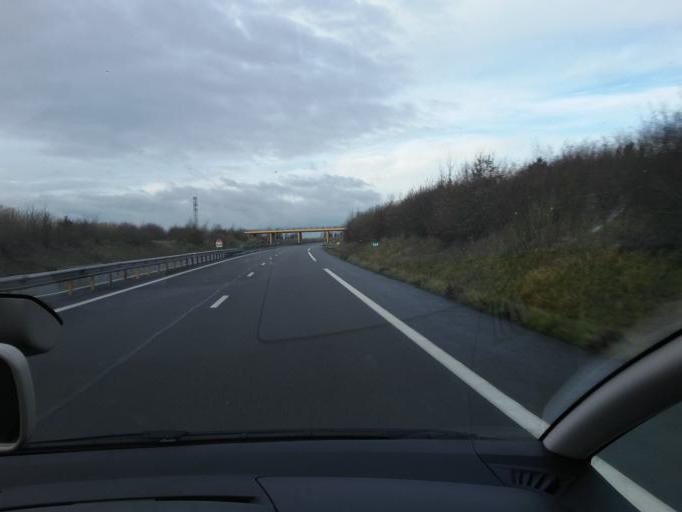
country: FR
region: Picardie
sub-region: Departement de la Somme
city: Rosieres-en-Santerre
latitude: 49.8538
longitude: 2.7136
